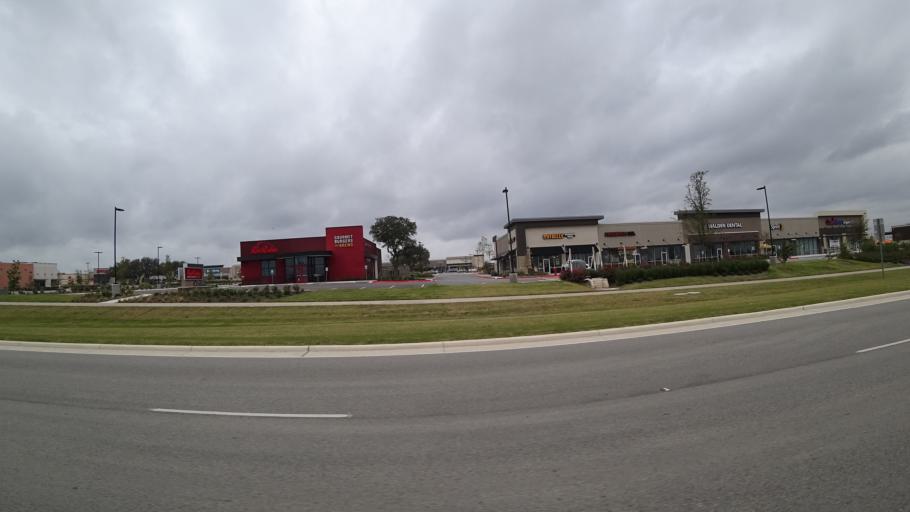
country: US
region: Texas
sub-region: Williamson County
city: Cedar Park
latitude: 30.5332
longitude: -97.8175
